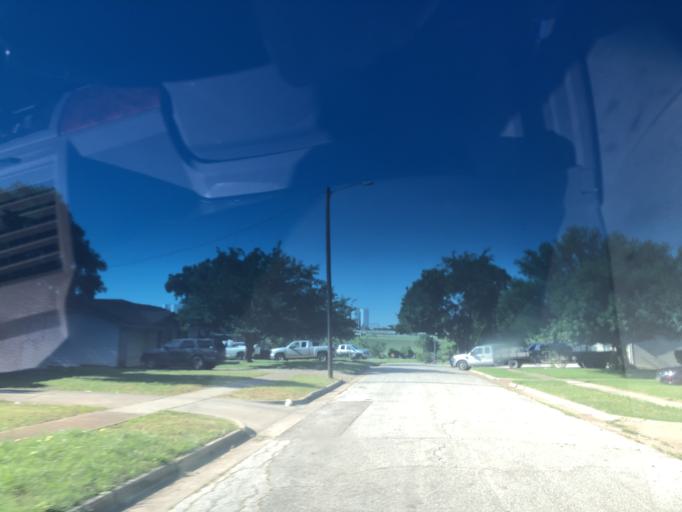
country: US
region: Texas
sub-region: Dallas County
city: Grand Prairie
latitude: 32.7286
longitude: -97.0364
